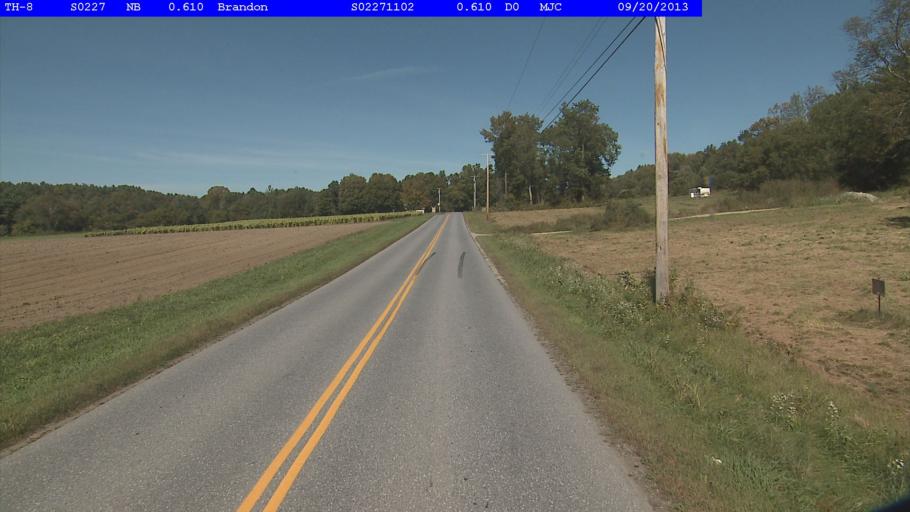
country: US
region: Vermont
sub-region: Rutland County
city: Brandon
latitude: 43.7832
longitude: -73.0530
